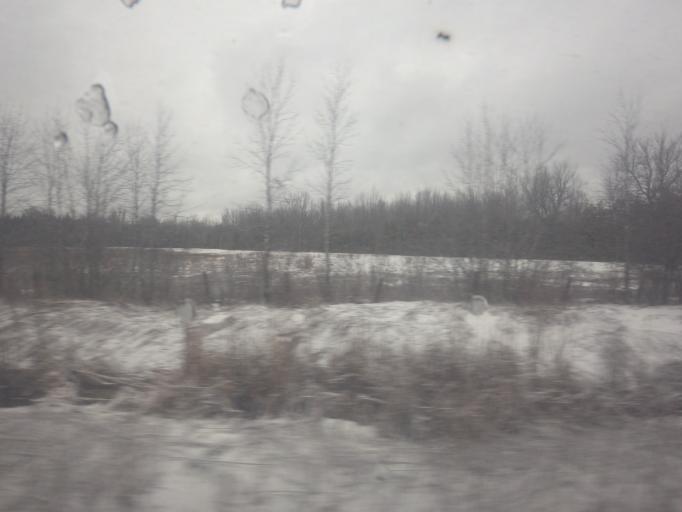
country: CA
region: Ontario
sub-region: Lanark County
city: Smiths Falls
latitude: 44.9323
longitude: -76.0268
